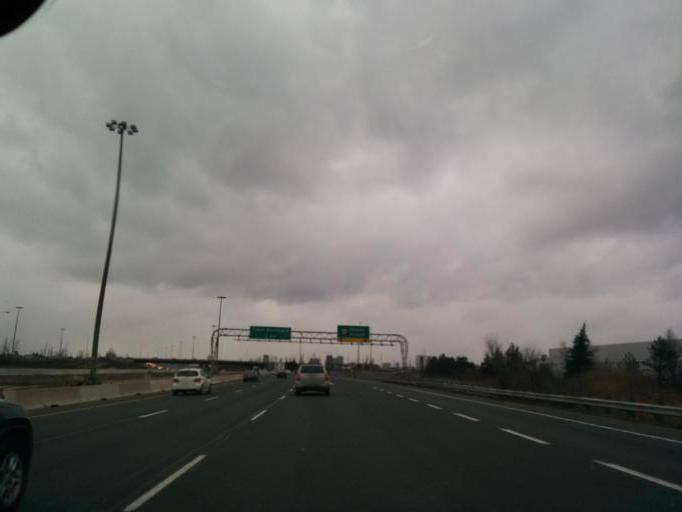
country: CA
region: Ontario
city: Brampton
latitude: 43.6818
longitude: -79.7075
